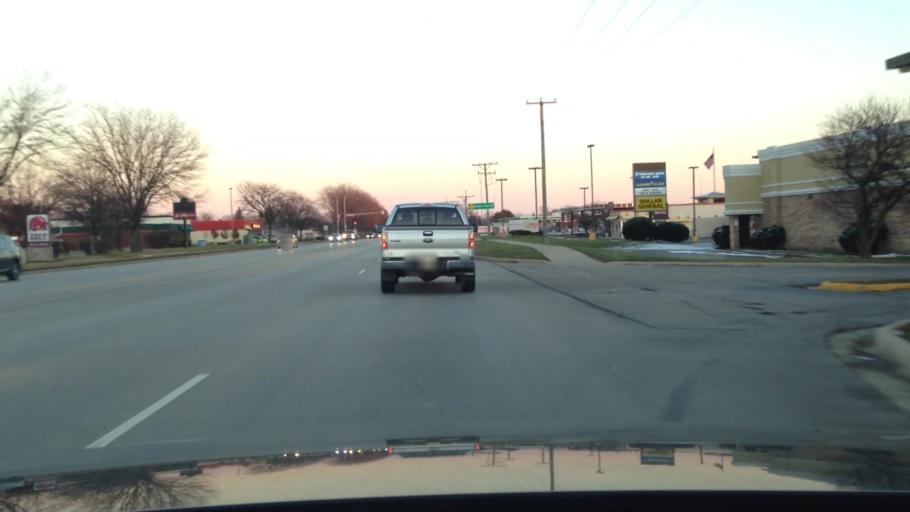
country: US
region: Illinois
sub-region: DuPage County
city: Carol Stream
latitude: 41.9408
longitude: -88.1537
